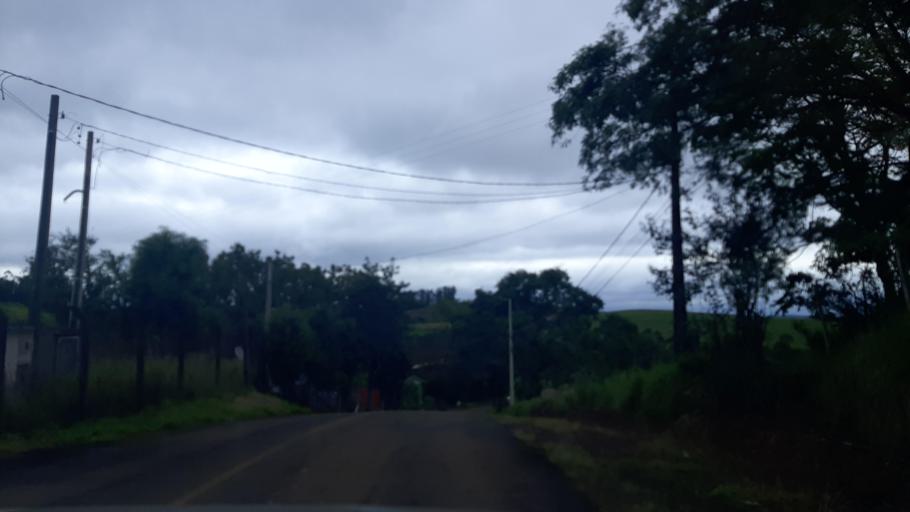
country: BR
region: Parana
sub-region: Ampere
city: Ampere
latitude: -26.0366
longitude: -53.4880
